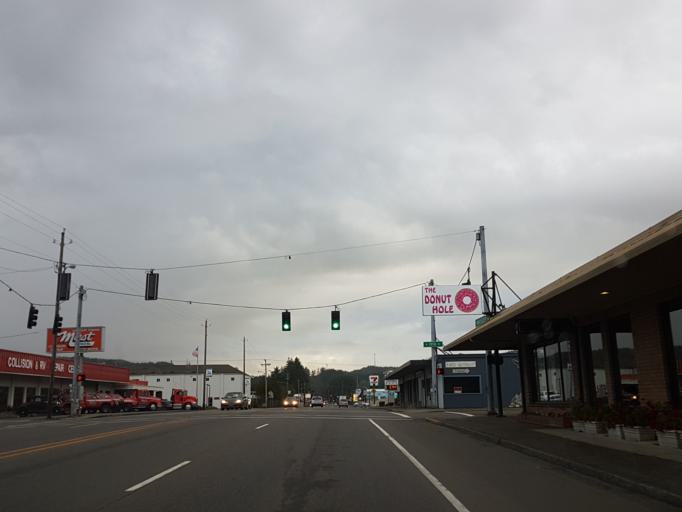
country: US
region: Oregon
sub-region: Douglas County
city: Reedsport
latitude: 43.6963
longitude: -124.1181
